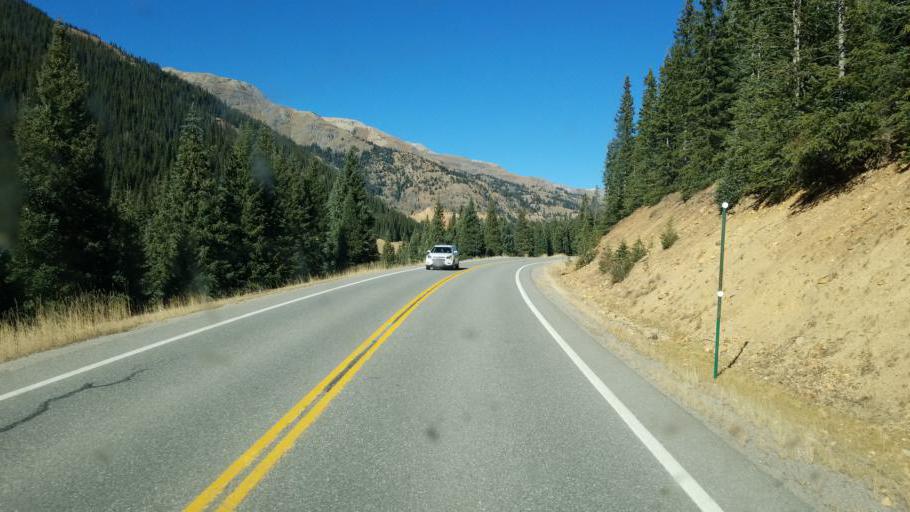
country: US
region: Colorado
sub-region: San Juan County
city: Silverton
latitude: 37.8540
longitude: -107.7253
